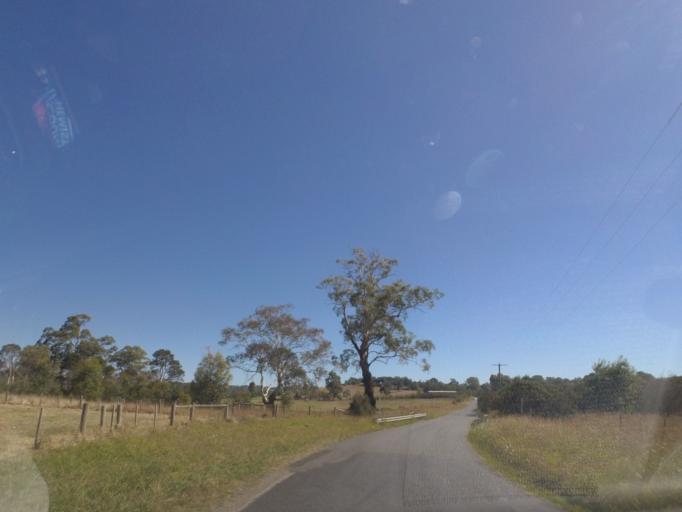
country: AU
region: Victoria
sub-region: Yarra Ranges
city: Chirnside Park
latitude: -37.7282
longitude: 145.2918
